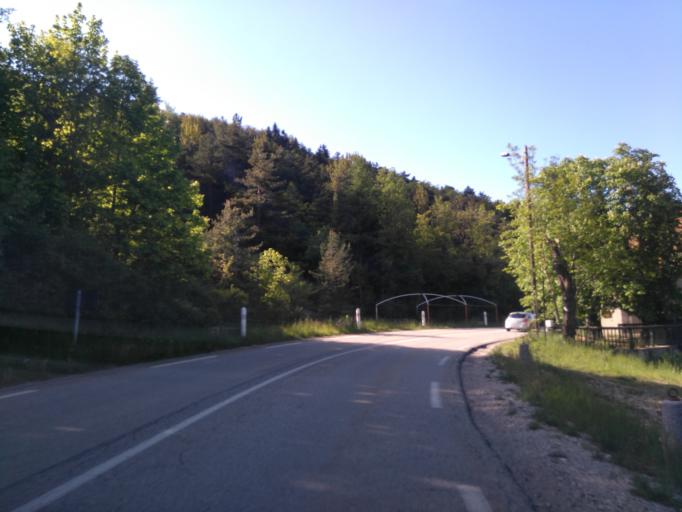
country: FR
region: Rhone-Alpes
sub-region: Departement de l'Isere
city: Mens
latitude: 44.7634
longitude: 5.6595
